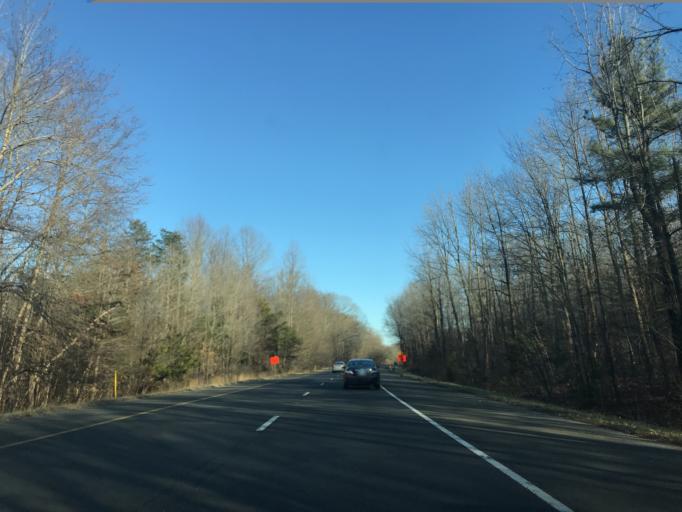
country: US
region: Maryland
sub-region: Prince George's County
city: Upper Marlboro
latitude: 38.8117
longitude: -76.7722
